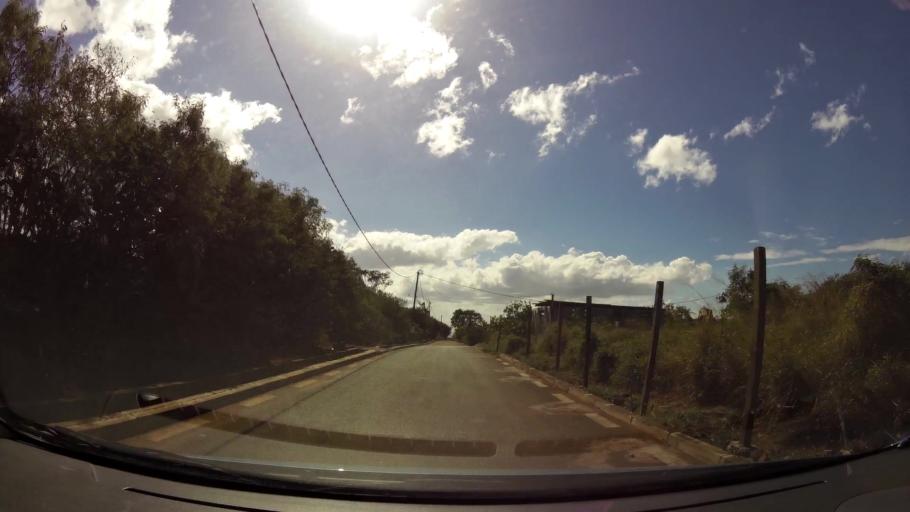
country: MU
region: Black River
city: Gros Cailloux
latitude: -20.2291
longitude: 57.4279
